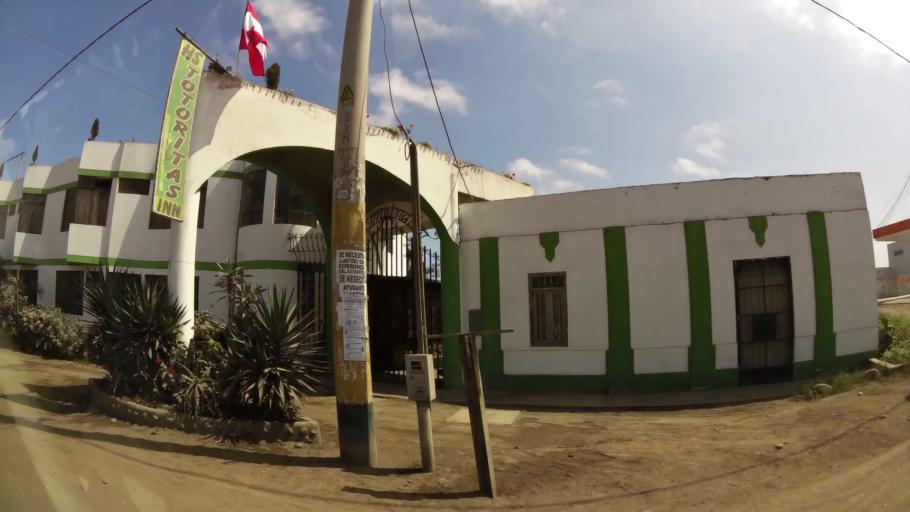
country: PE
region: Lima
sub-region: Provincia de Canete
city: Mala
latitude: -12.6616
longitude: -76.6384
